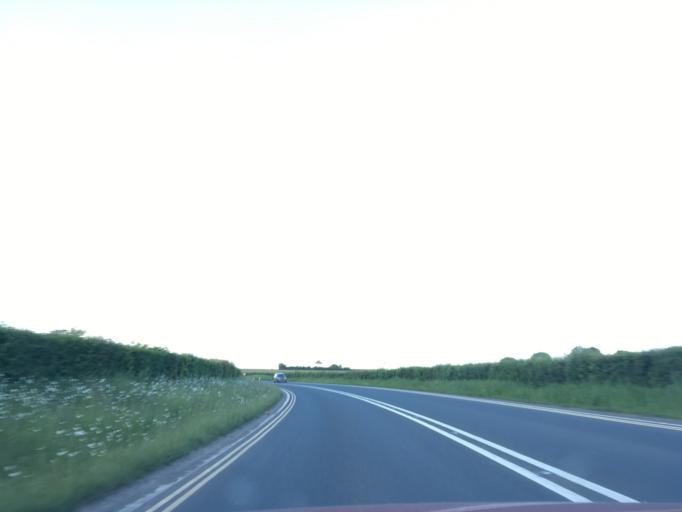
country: GB
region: England
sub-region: North Somerset
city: Butcombe
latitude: 51.3796
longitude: -2.7043
